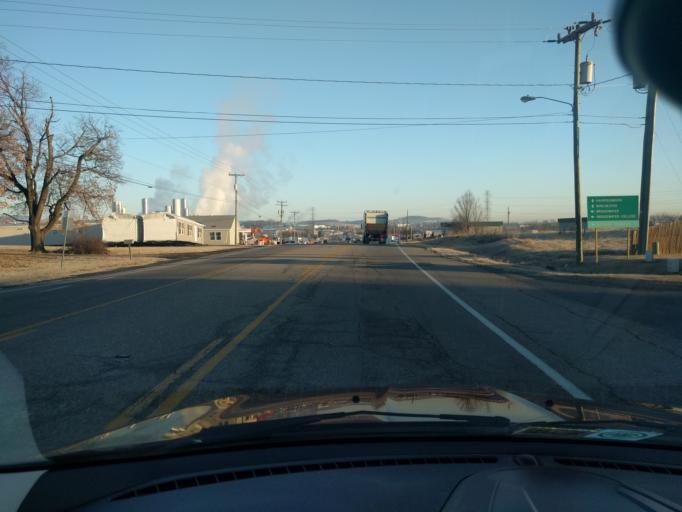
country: US
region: Virginia
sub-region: Rockingham County
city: Bridgewater
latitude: 38.3638
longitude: -78.9373
